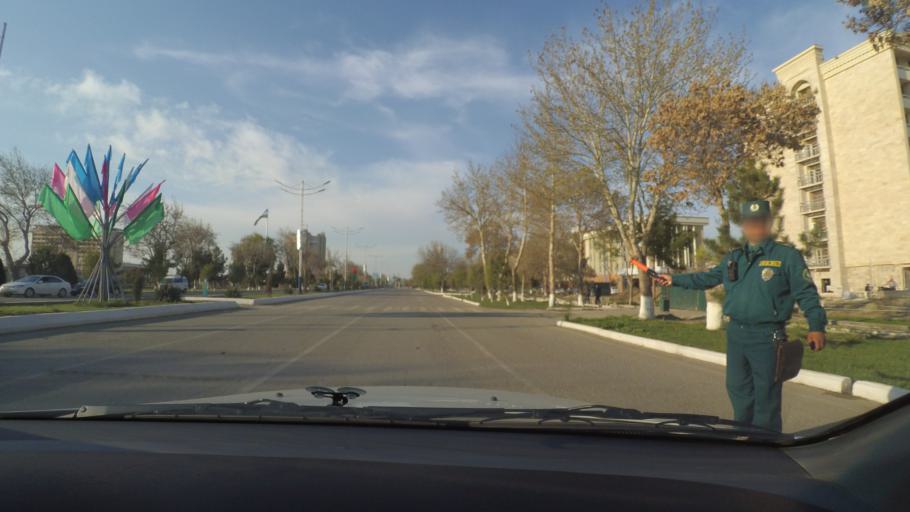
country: UZ
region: Bukhara
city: Bukhara
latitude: 39.7634
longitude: 64.4243
